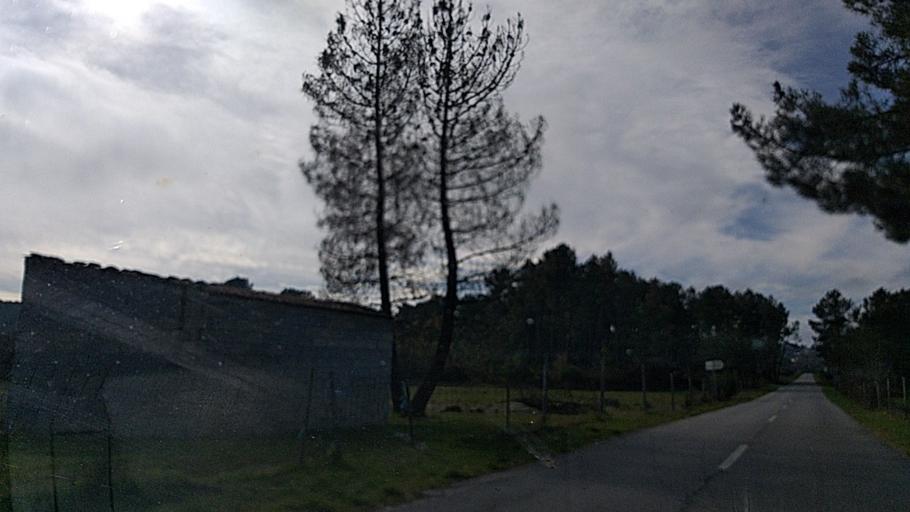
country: PT
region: Guarda
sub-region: Fornos de Algodres
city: Fornos de Algodres
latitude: 40.6676
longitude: -7.5296
